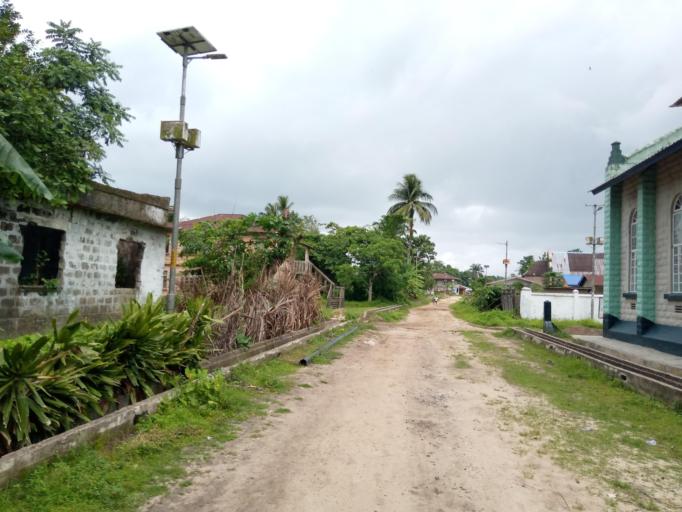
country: SL
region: Southern Province
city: Bonthe
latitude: 7.5321
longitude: -12.5032
